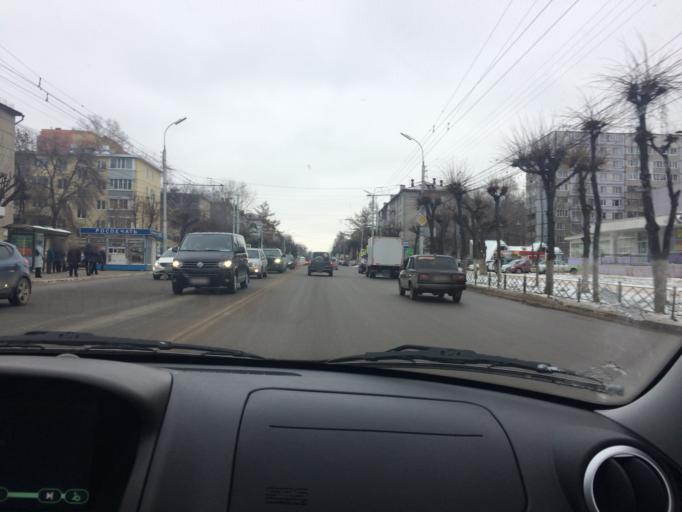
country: RU
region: Rjazan
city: Ryazan'
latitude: 54.6233
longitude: 39.7193
